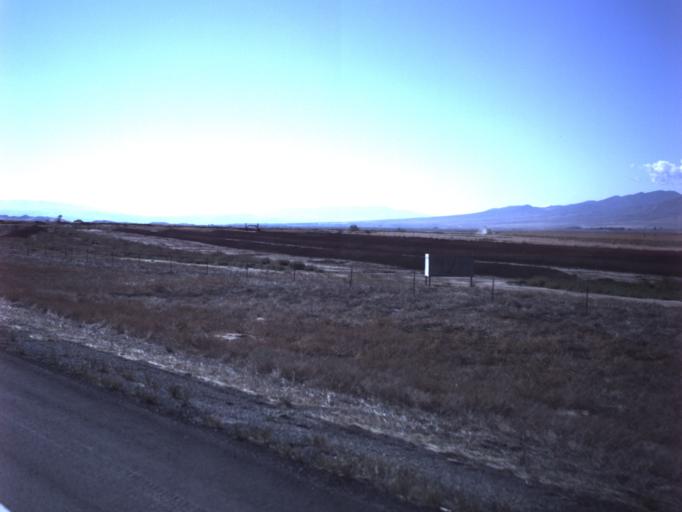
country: US
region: Utah
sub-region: Sanpete County
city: Gunnison
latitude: 39.2571
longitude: -111.8625
